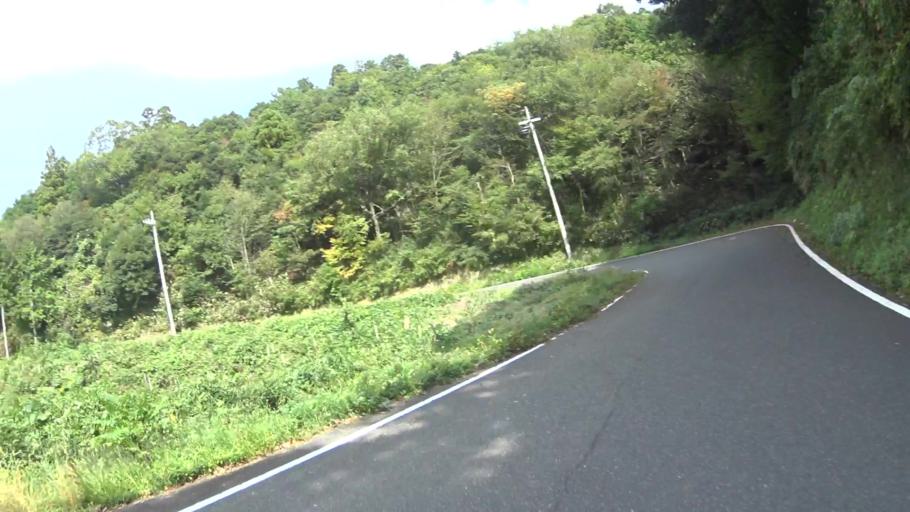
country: JP
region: Kyoto
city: Miyazu
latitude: 35.6799
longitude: 135.2674
